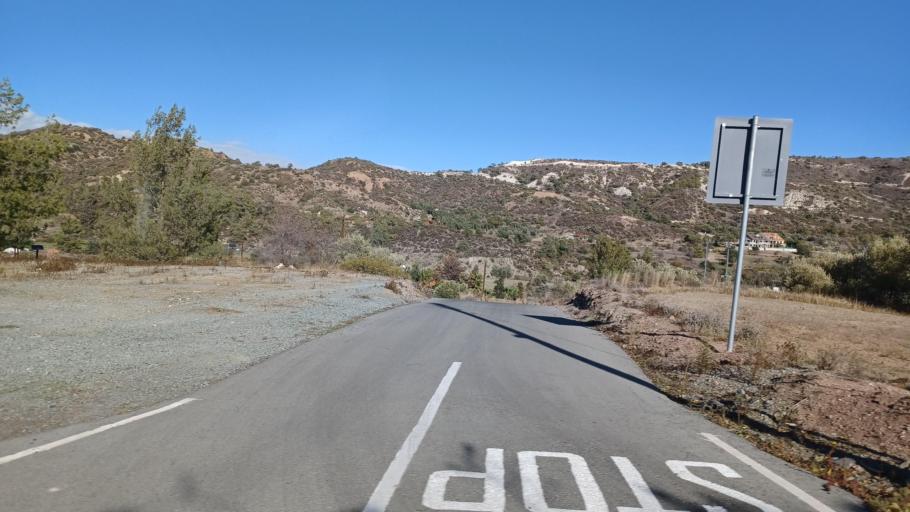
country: CY
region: Limassol
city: Pyrgos
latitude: 34.7828
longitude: 33.2497
